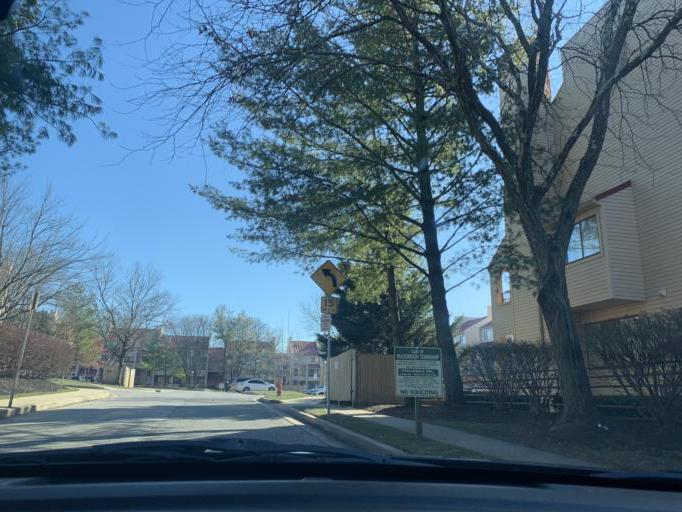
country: US
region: Maryland
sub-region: Baltimore County
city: Garrison
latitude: 39.4020
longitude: -76.7588
